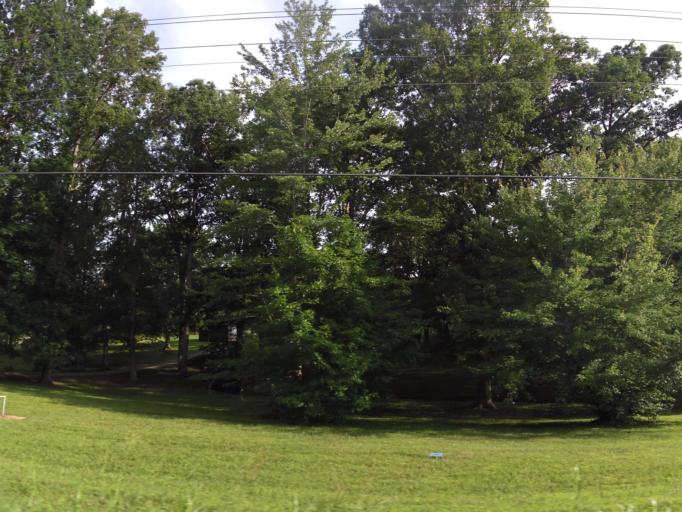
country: US
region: Tennessee
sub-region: Dickson County
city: Dickson
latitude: 36.0886
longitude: -87.4596
